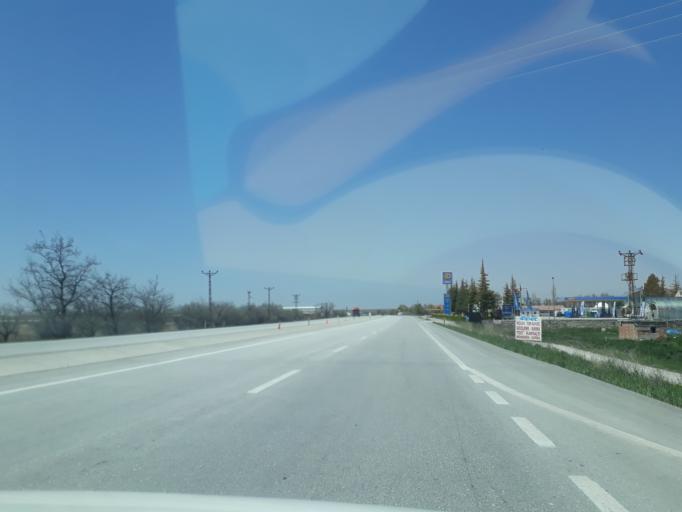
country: TR
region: Konya
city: Karapinar
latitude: 37.7164
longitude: 33.4913
